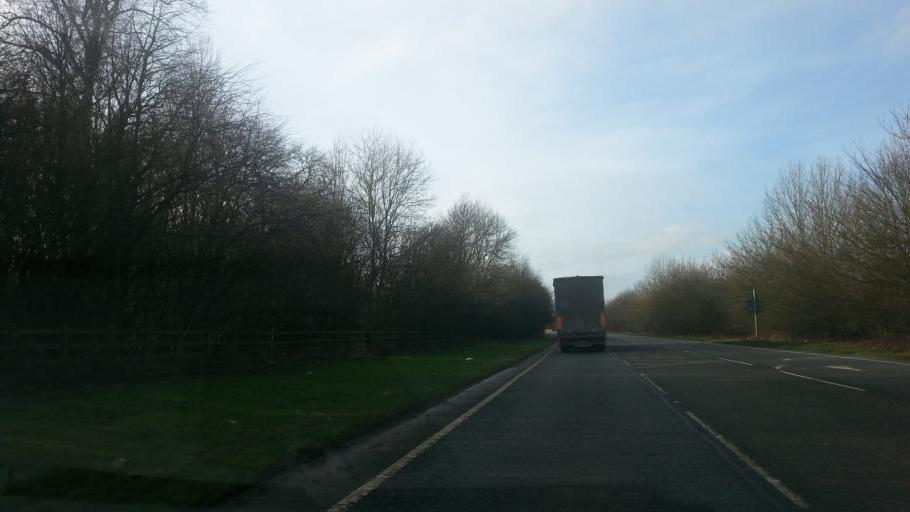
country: GB
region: England
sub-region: District of Rutland
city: Ridlington
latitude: 52.5977
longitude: -0.7933
